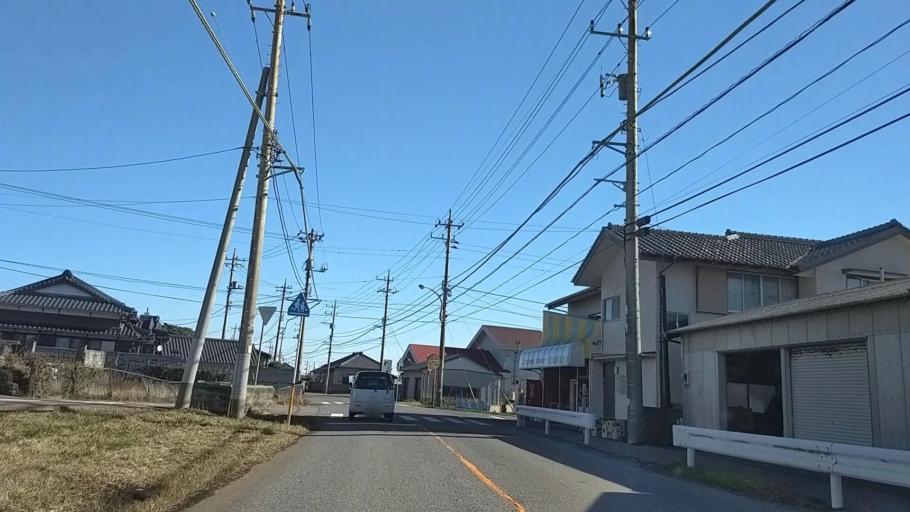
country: JP
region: Chiba
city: Tateyama
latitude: 34.9070
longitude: 139.8817
